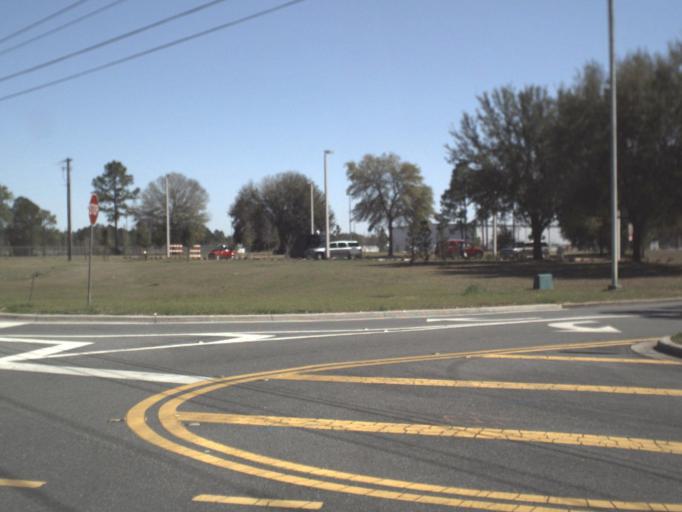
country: US
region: Florida
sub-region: Leon County
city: Tallahassee
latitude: 30.3978
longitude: -84.3424
